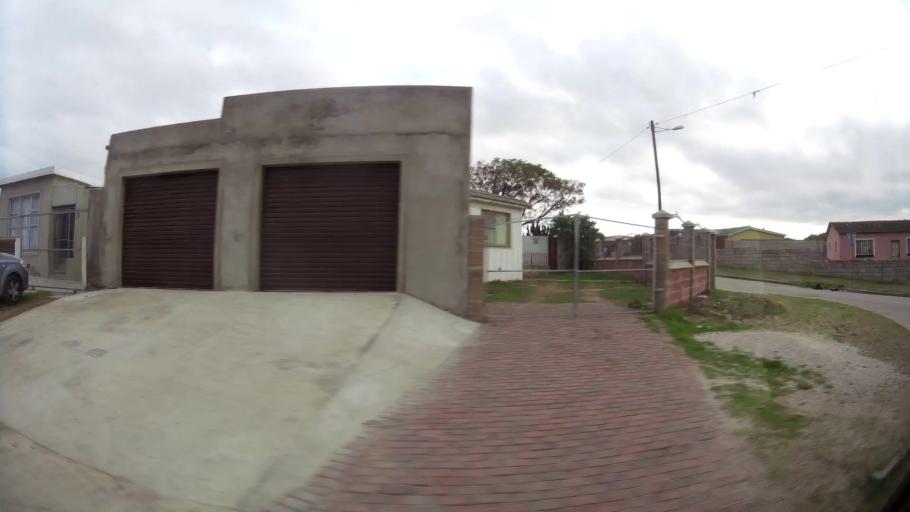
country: ZA
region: Eastern Cape
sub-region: Nelson Mandela Bay Metropolitan Municipality
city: Port Elizabeth
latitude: -33.9133
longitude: 25.5534
